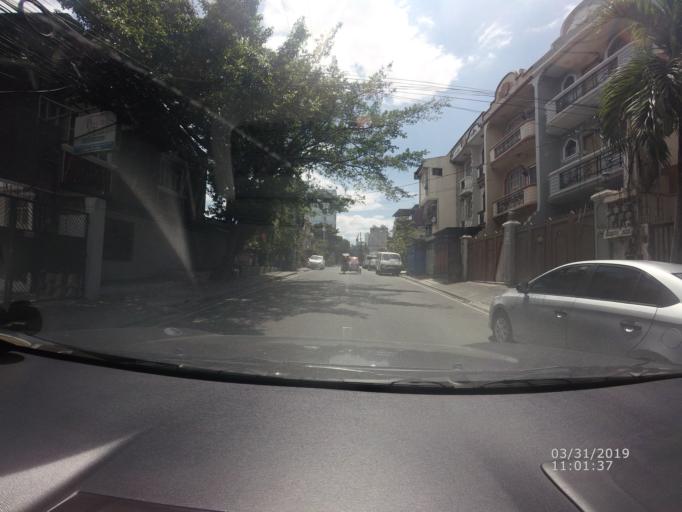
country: PH
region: Metro Manila
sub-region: Mandaluyong
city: Mandaluyong City
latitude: 14.5782
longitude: 121.0388
